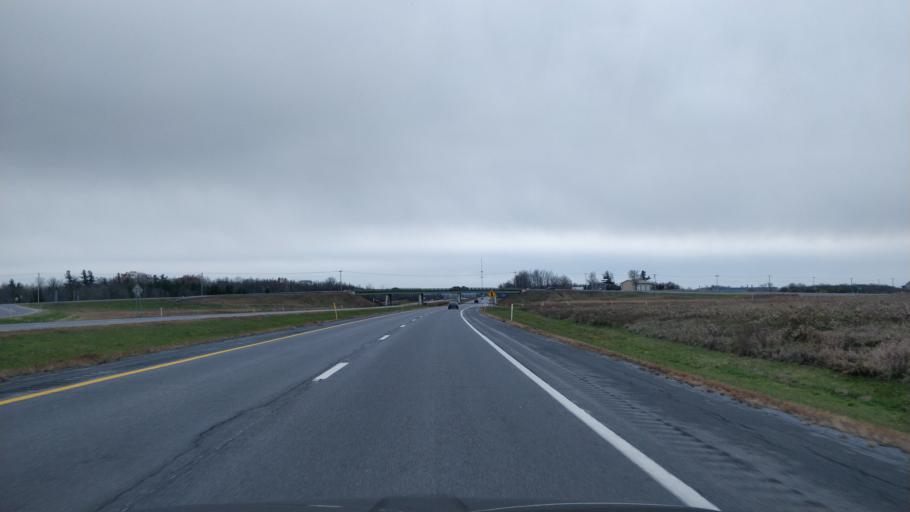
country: US
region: New York
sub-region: Jefferson County
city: Watertown
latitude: 44.0385
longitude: -75.9142
